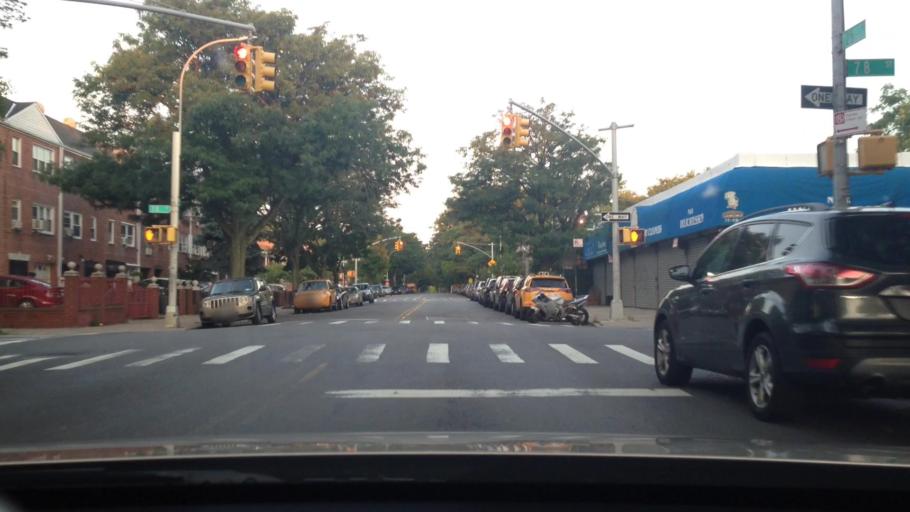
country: US
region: New York
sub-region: Queens County
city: Long Island City
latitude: 40.7627
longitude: -73.8902
